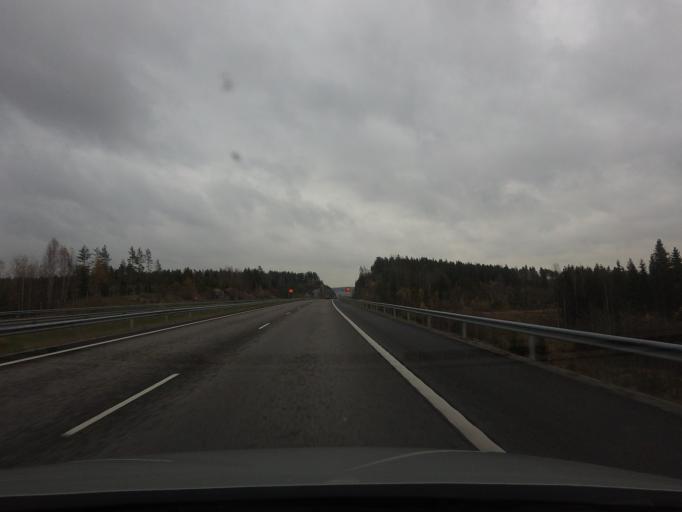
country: FI
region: Varsinais-Suomi
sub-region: Salo
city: Halikko
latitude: 60.4336
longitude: 22.9843
